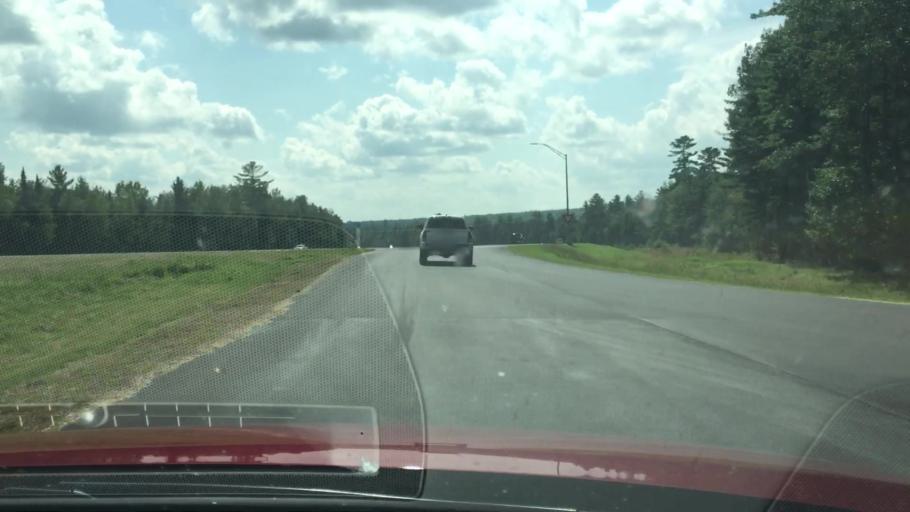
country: US
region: Maine
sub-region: Penobscot County
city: Medway
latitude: 45.5950
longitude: -68.5392
